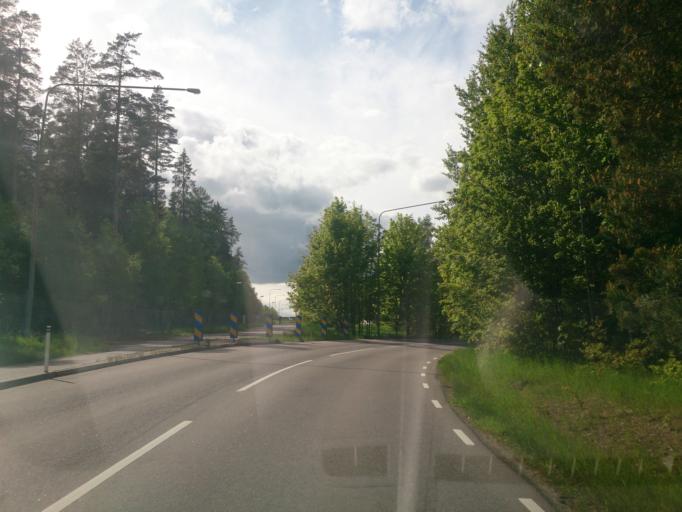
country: SE
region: OEstergoetland
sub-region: Linkopings Kommun
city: Malmslatt
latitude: 58.4095
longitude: 15.5414
